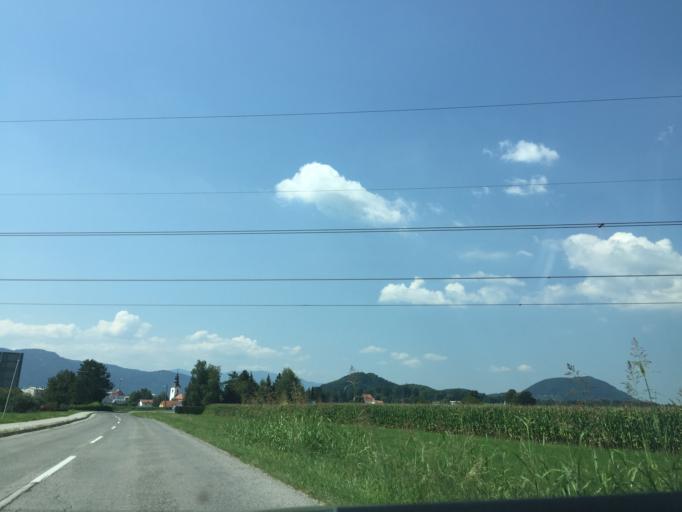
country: SI
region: Polzela
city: Polzela
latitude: 46.2762
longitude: 15.0841
